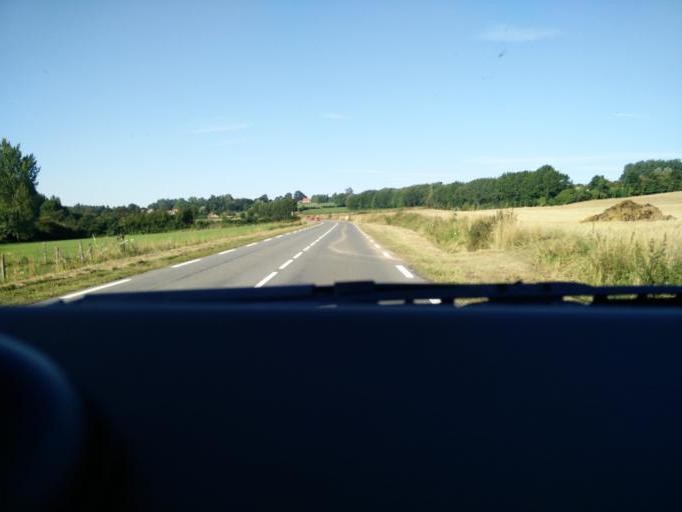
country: FR
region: Nord-Pas-de-Calais
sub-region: Departement du Pas-de-Calais
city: Camblain-Chatelain
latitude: 50.4432
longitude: 2.4610
